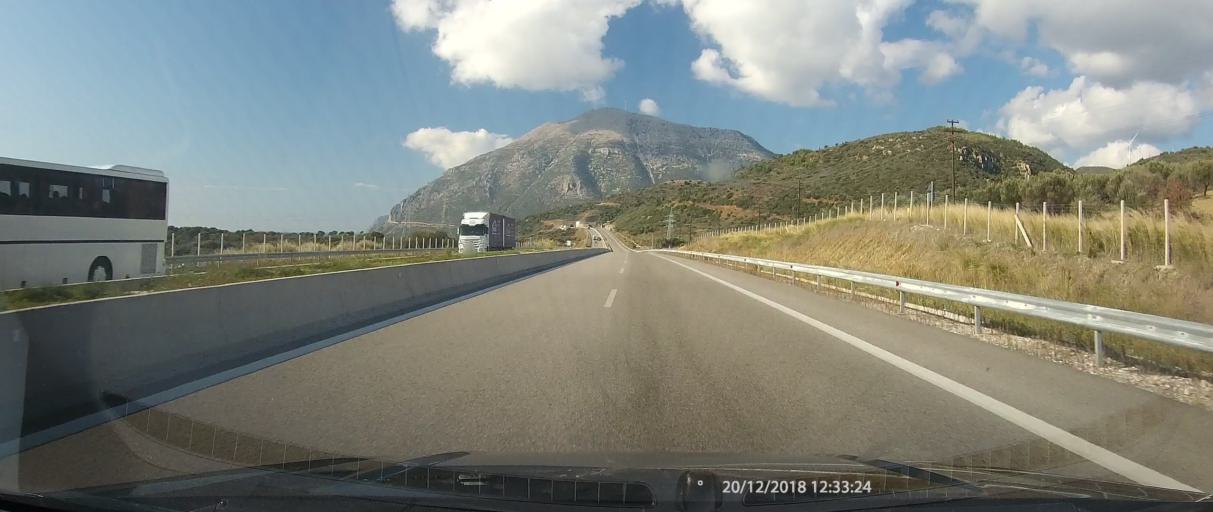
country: GR
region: West Greece
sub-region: Nomos Aitolias kai Akarnanias
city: Antirrio
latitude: 38.3502
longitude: 21.7428
